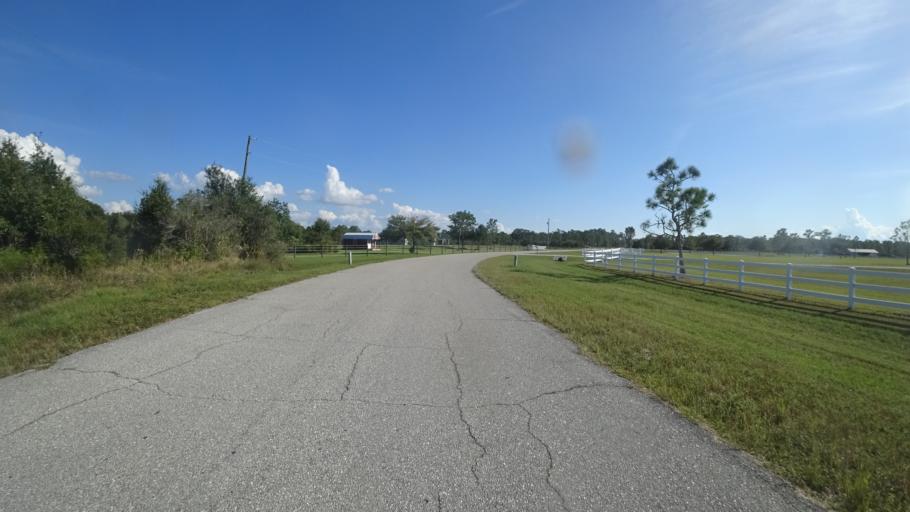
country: US
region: Florida
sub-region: Sarasota County
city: Lake Sarasota
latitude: 27.3960
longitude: -82.2837
